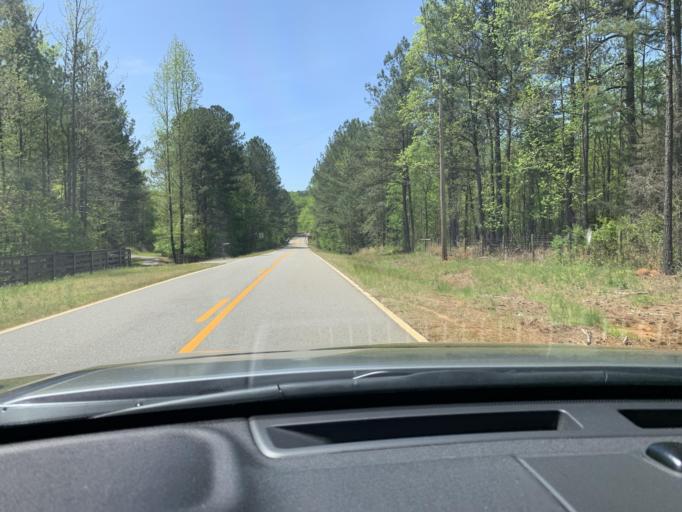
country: US
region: Georgia
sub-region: Oconee County
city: Bogart
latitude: 33.8561
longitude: -83.5734
